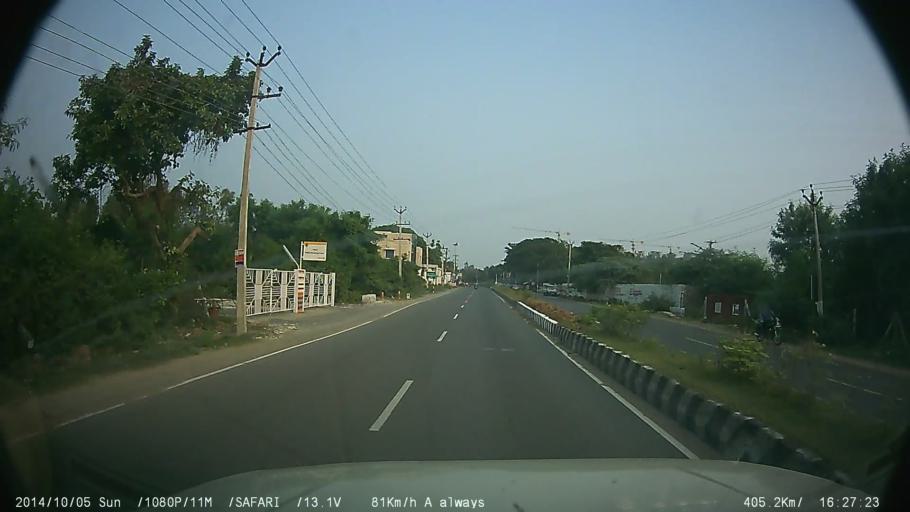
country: IN
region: Tamil Nadu
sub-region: Kancheepuram
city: Vengavasal
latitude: 12.8006
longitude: 80.1965
